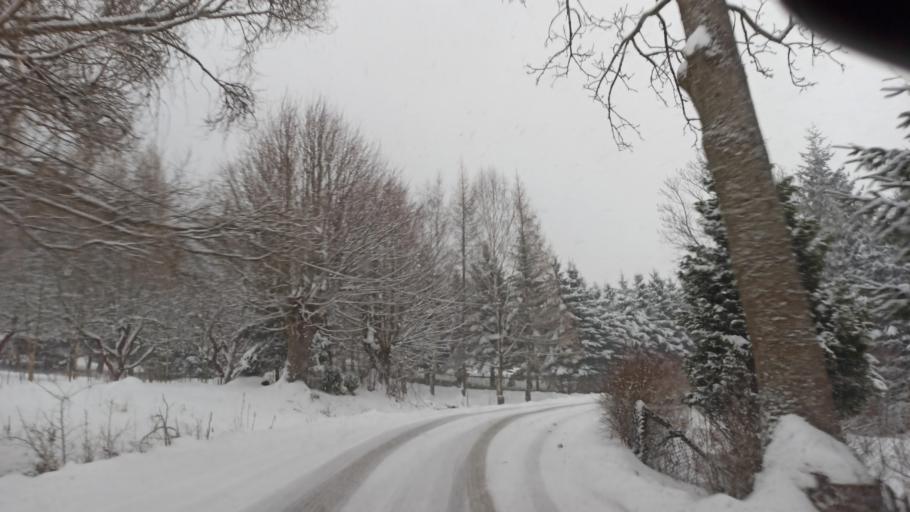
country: PL
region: Lower Silesian Voivodeship
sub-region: Powiat klodzki
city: Ludwikowice Klodzkie
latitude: 50.6488
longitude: 16.4798
